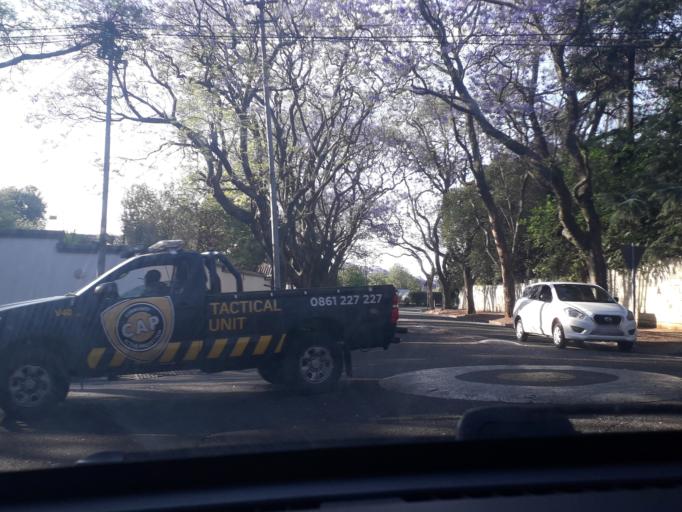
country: ZA
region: Gauteng
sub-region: City of Johannesburg Metropolitan Municipality
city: Johannesburg
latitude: -26.1536
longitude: 28.0376
